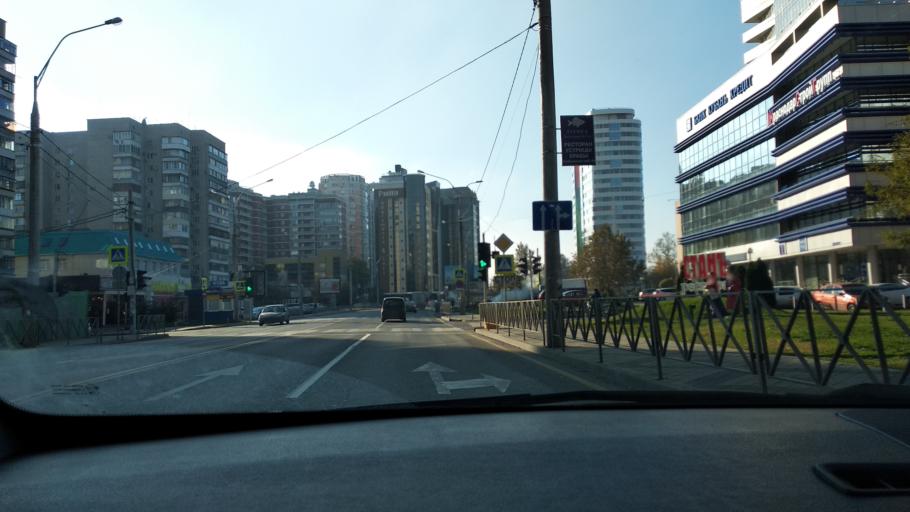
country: RU
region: Krasnodarskiy
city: Krasnodar
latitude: 45.0198
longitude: 38.9598
